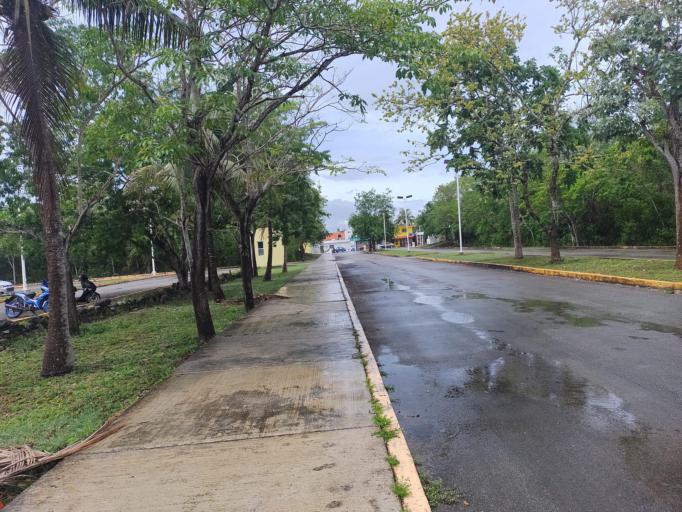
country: MX
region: Quintana Roo
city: San Miguel de Cozumel
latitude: 20.4900
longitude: -86.9402
